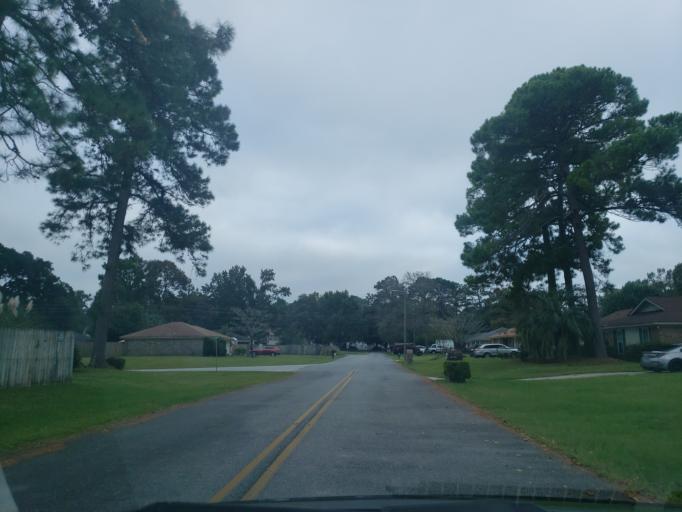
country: US
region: Georgia
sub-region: Chatham County
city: Montgomery
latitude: 31.9507
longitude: -81.1110
